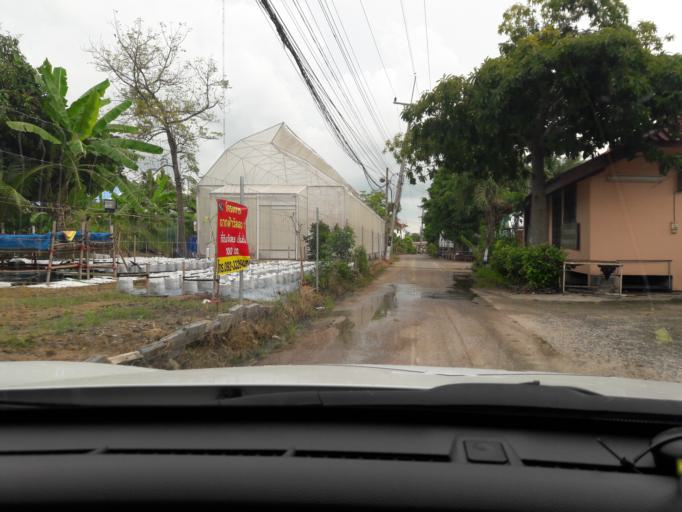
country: TH
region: Nakhon Sawan
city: Tak Fa
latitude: 15.3496
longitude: 100.5002
